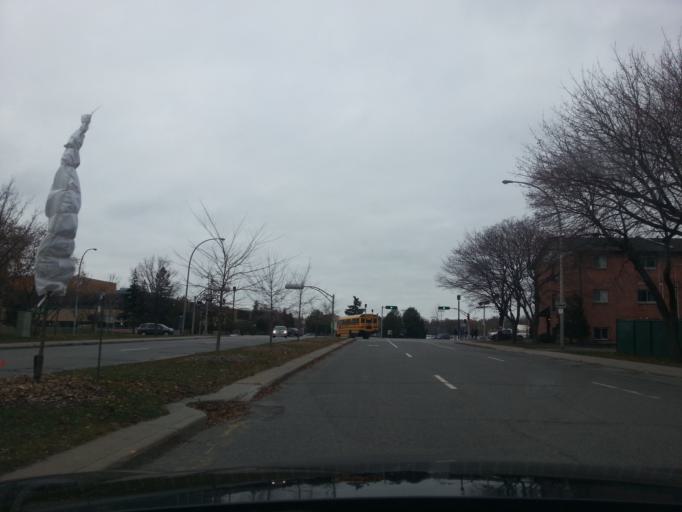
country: CA
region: Ontario
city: Ottawa
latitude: 45.4368
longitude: -75.7213
